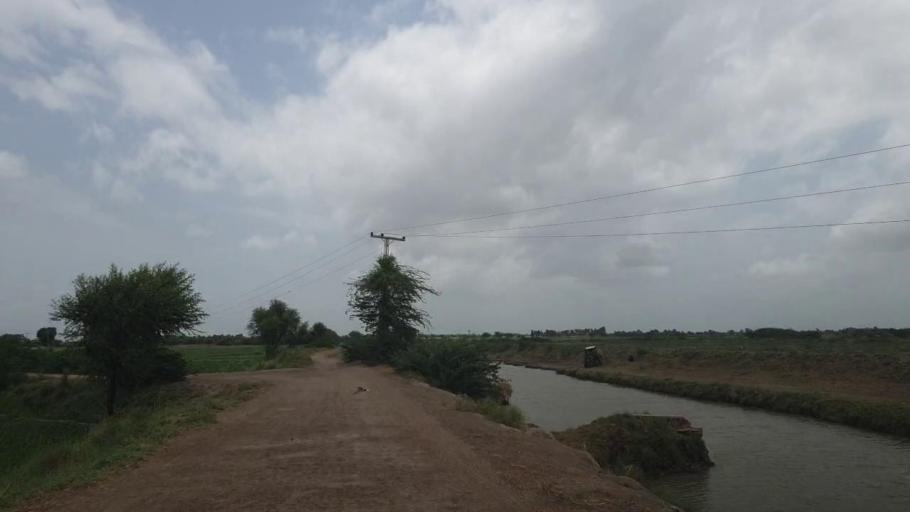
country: PK
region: Sindh
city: Badin
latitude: 24.6631
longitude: 68.8926
